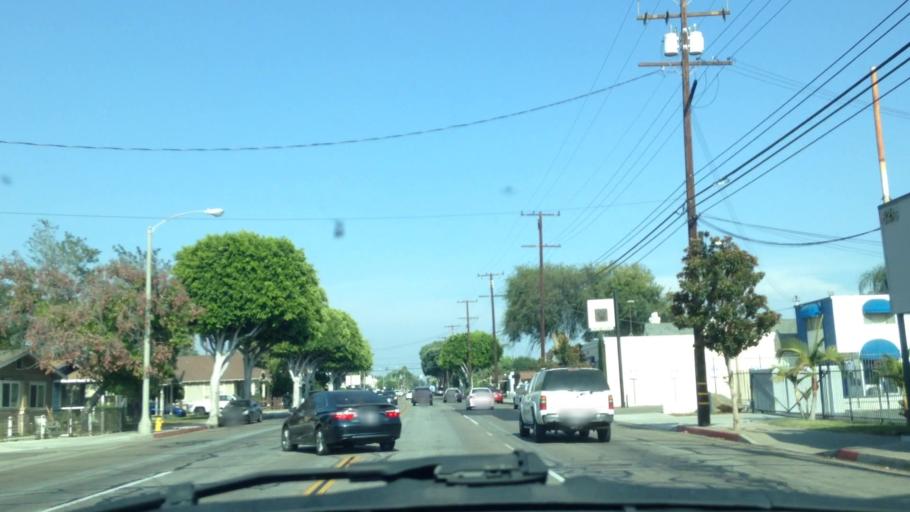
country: US
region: California
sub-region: Orange County
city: Fullerton
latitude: 33.8704
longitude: -117.9111
